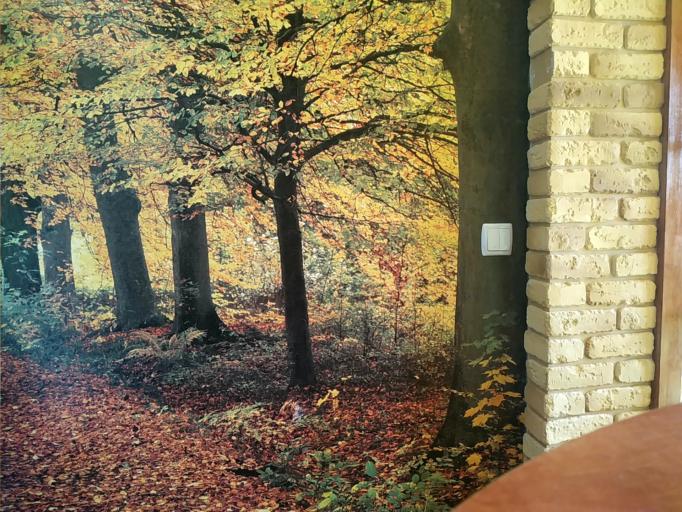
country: RU
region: Jaroslavl
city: Kukoboy
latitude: 58.9141
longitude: 39.6816
